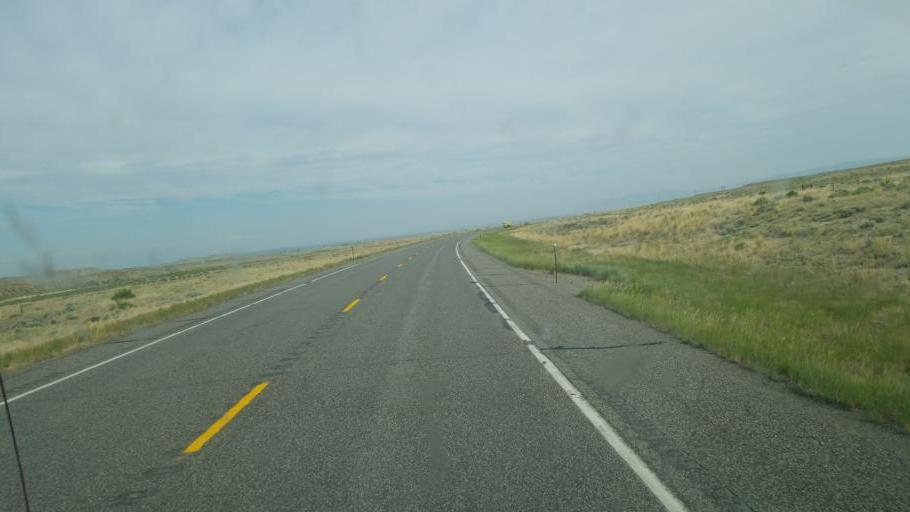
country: US
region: Wyoming
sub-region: Fremont County
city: Riverton
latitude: 43.2244
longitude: -108.0473
